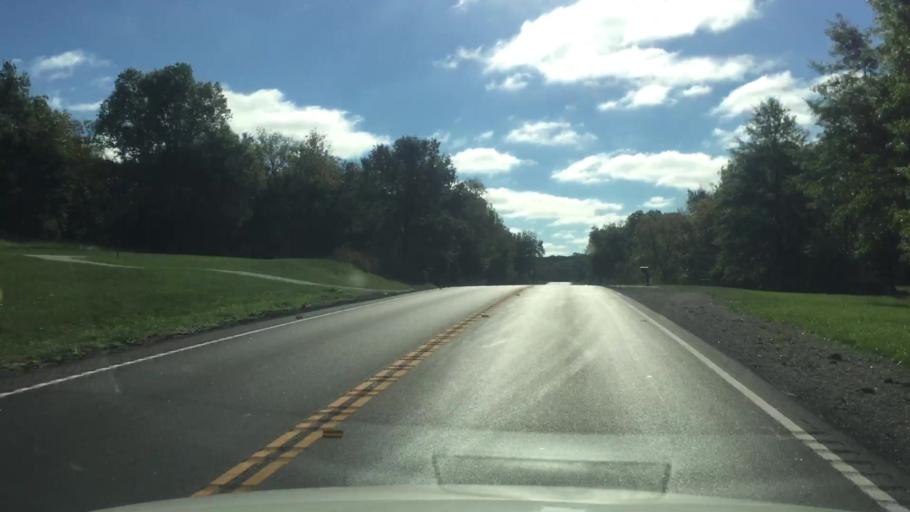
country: US
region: Missouri
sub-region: Howard County
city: New Franklin
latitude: 38.9915
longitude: -92.5624
